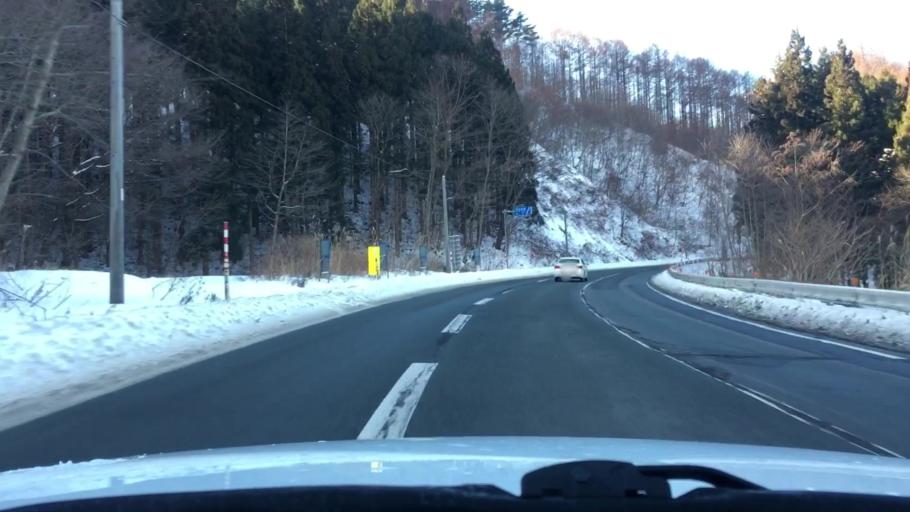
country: JP
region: Iwate
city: Morioka-shi
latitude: 39.6657
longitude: 141.3317
